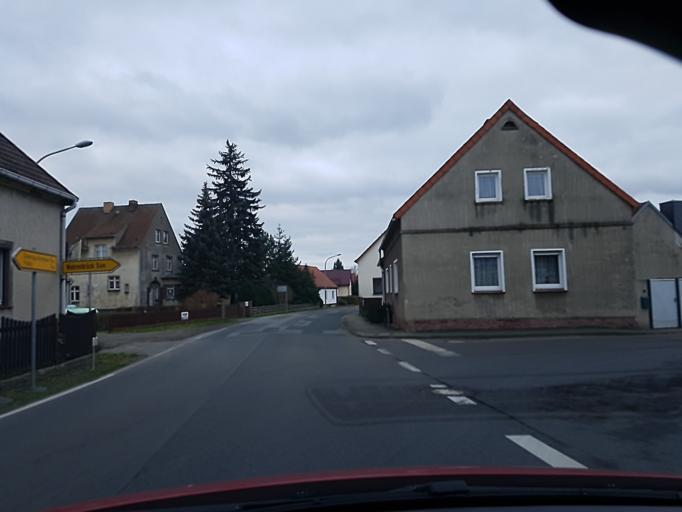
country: DE
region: Brandenburg
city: Trobitz
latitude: 51.5596
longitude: 13.4189
